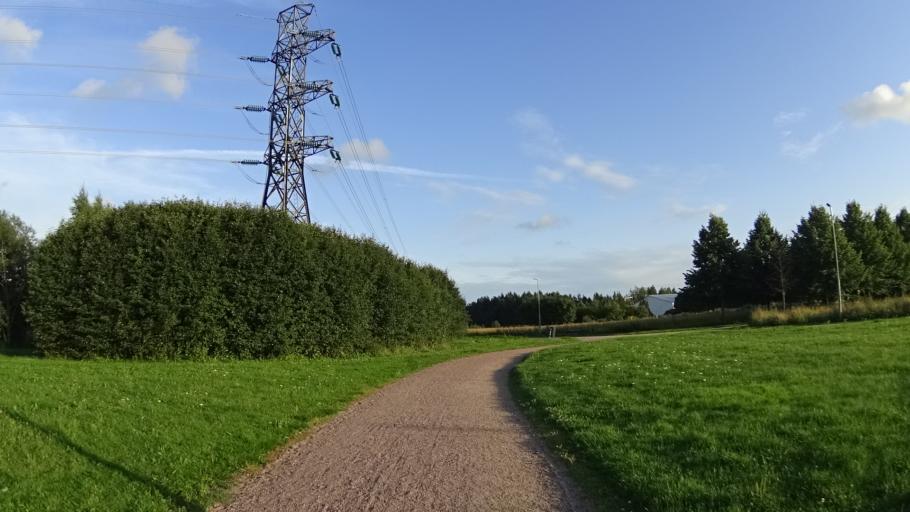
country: FI
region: Uusimaa
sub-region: Helsinki
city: Teekkarikylae
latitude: 60.2395
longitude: 24.8638
